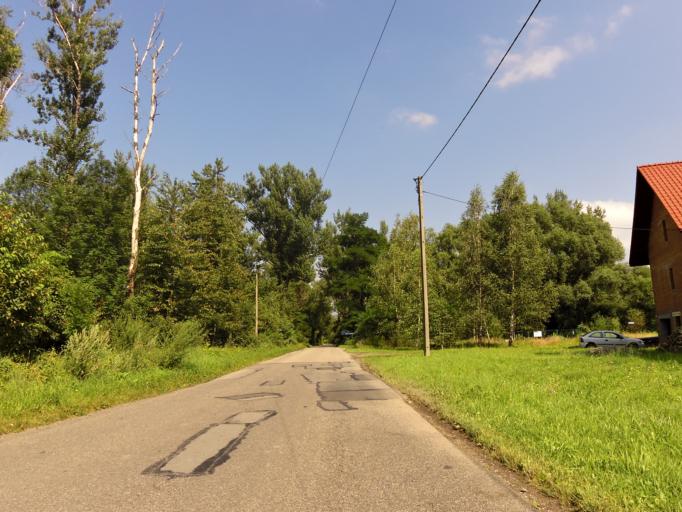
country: PL
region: Silesian Voivodeship
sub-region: Powiat zywiecki
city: Ciecina
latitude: 49.6231
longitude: 19.1558
